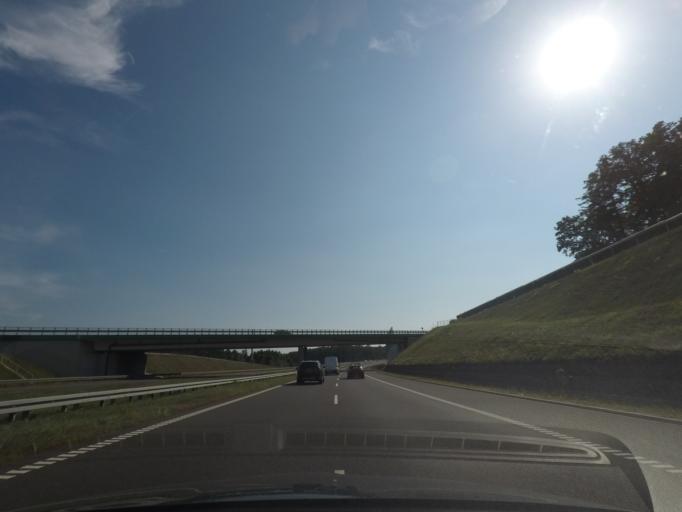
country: PL
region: Silesian Voivodeship
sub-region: Zory
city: Zory
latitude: 50.0535
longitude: 18.6457
